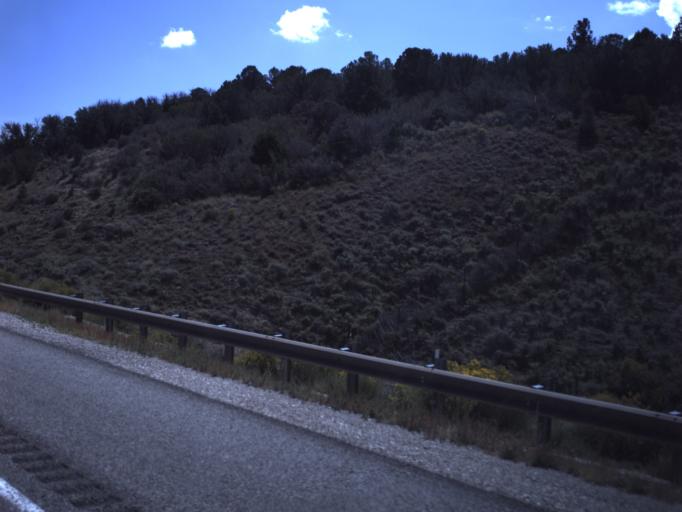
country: US
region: Utah
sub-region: Wayne County
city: Loa
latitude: 38.7782
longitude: -111.4821
